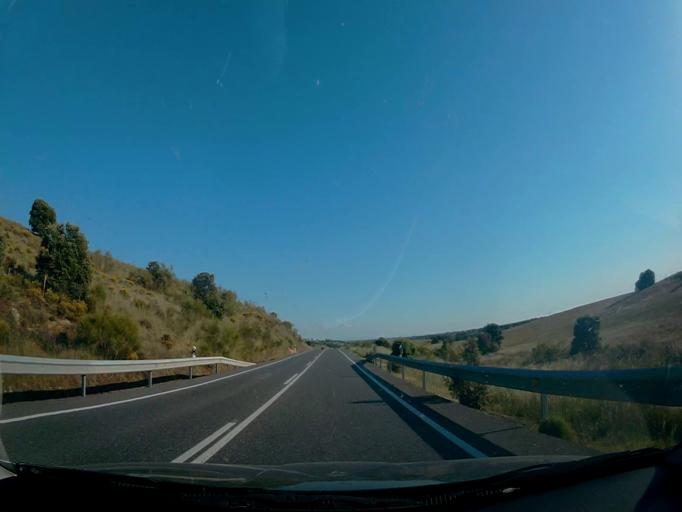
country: ES
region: Castille-La Mancha
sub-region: Province of Toledo
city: Almorox
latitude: 40.2099
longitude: -4.3966
